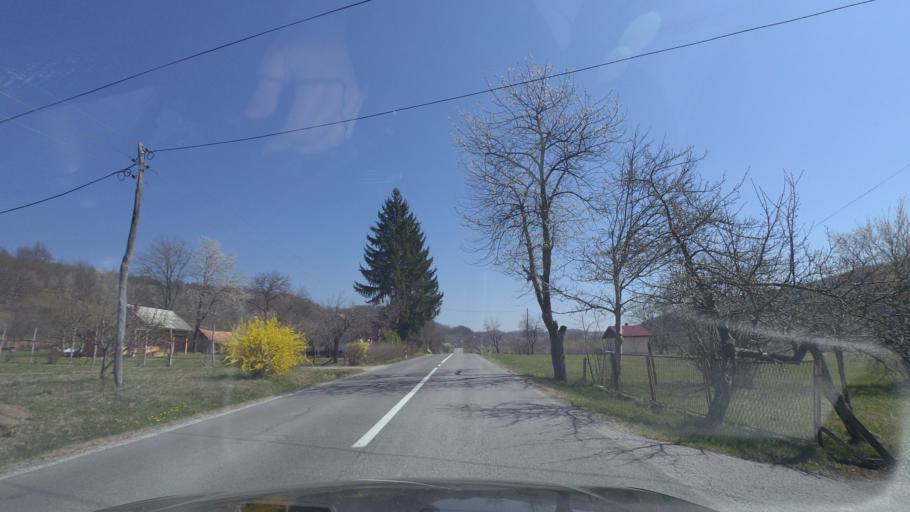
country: HR
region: Karlovacka
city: Vojnic
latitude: 45.3788
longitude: 15.6354
